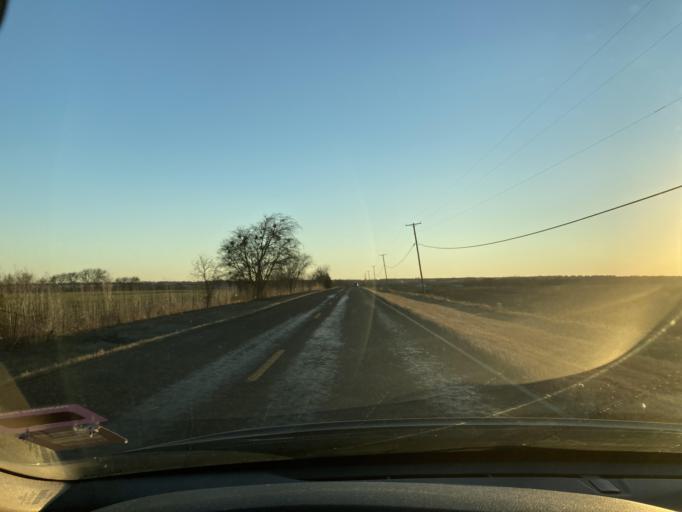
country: US
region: Texas
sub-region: Ellis County
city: Waxahachie
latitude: 32.3638
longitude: -96.8654
